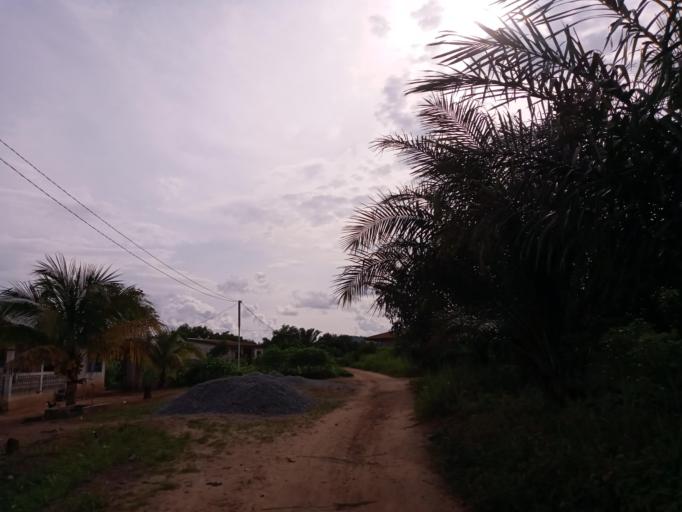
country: SL
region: Northern Province
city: Bumbuna
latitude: 9.0499
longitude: -11.7557
